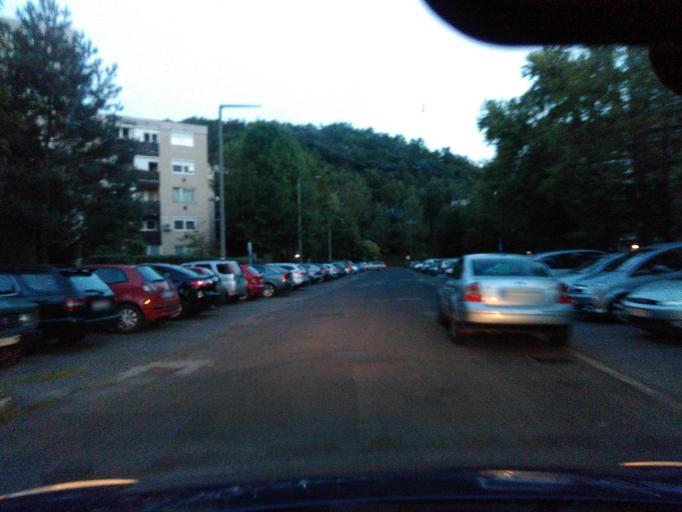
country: HU
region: Nograd
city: Somoskoujfalu
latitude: 48.1311
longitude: 19.8153
